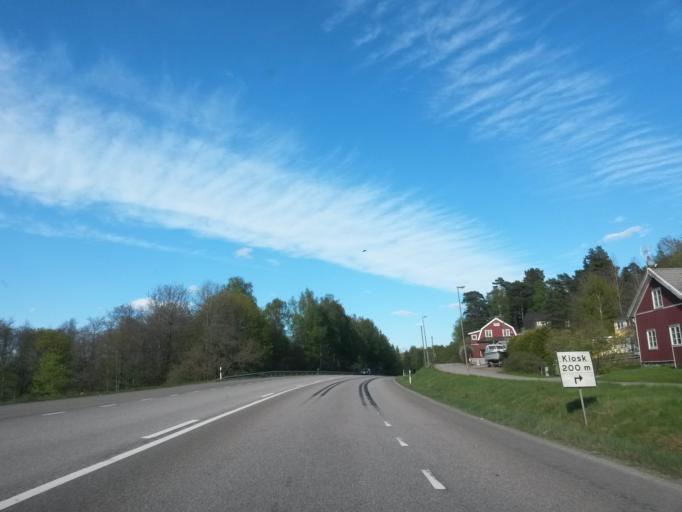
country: SE
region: Vaestra Goetaland
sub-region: Alingsas Kommun
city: Alingsas
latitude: 57.9333
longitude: 12.5713
